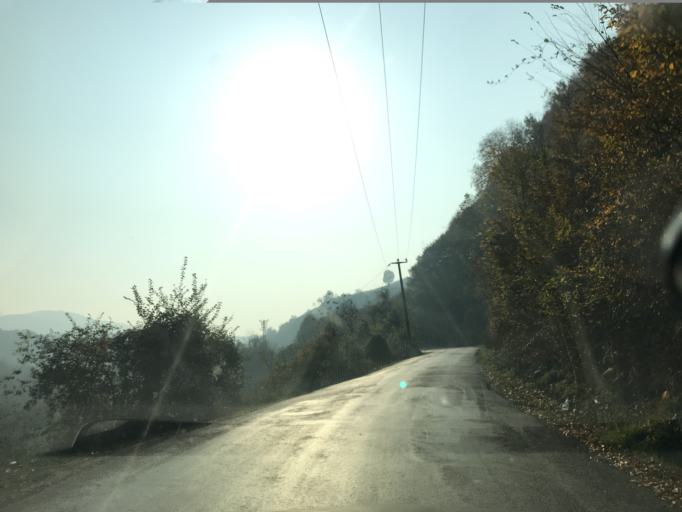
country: TR
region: Duzce
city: Cumayeri
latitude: 40.9119
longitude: 30.9443
